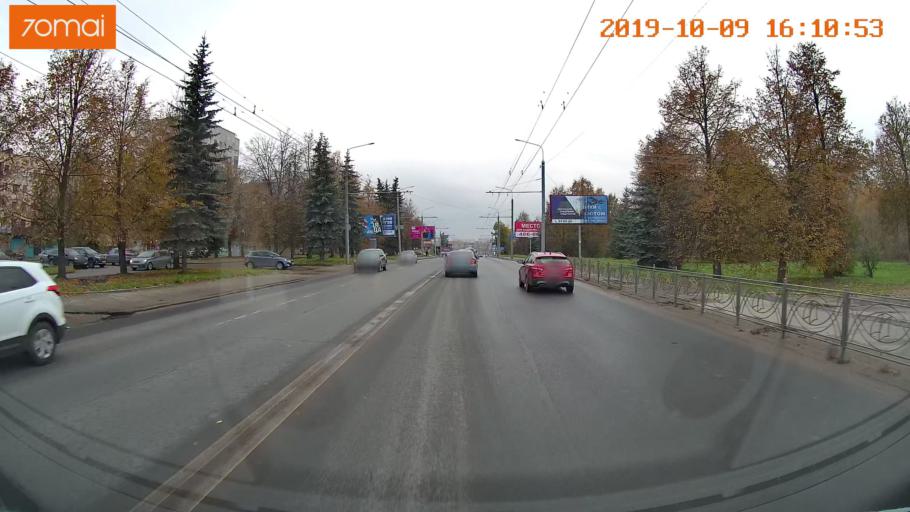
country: RU
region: Kostroma
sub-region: Kostromskoy Rayon
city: Kostroma
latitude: 57.7602
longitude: 40.9501
